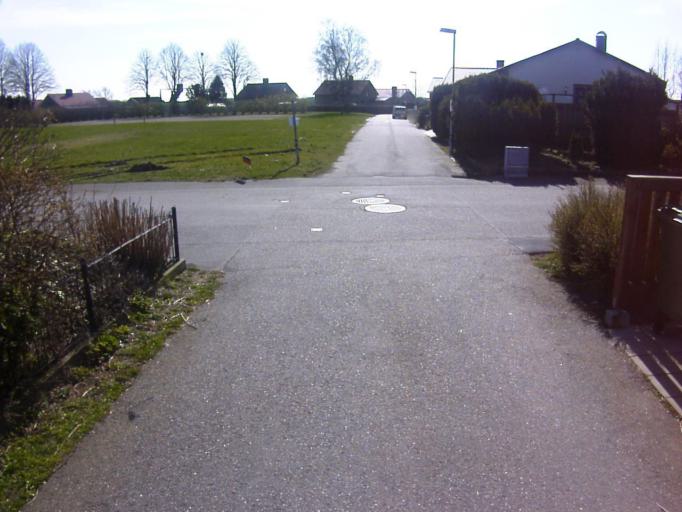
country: SE
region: Skane
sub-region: Kavlinge Kommun
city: Kaevlinge
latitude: 55.7906
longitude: 13.0886
